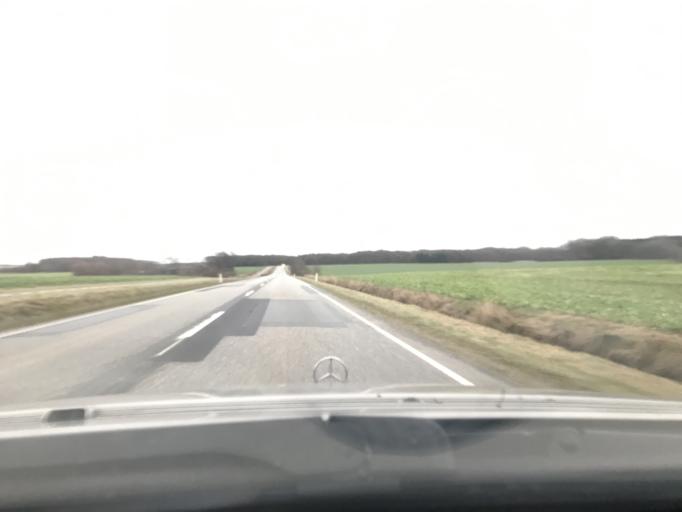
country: DK
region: South Denmark
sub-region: Tonder Kommune
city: Toftlund
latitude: 55.1505
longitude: 9.1047
